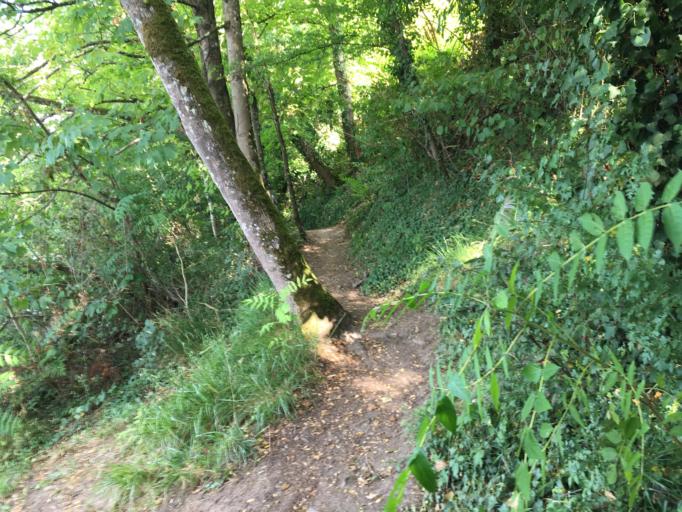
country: FR
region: Centre
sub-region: Departement d'Indre-et-Loire
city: Saint-Avertin
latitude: 47.3689
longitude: 0.7401
